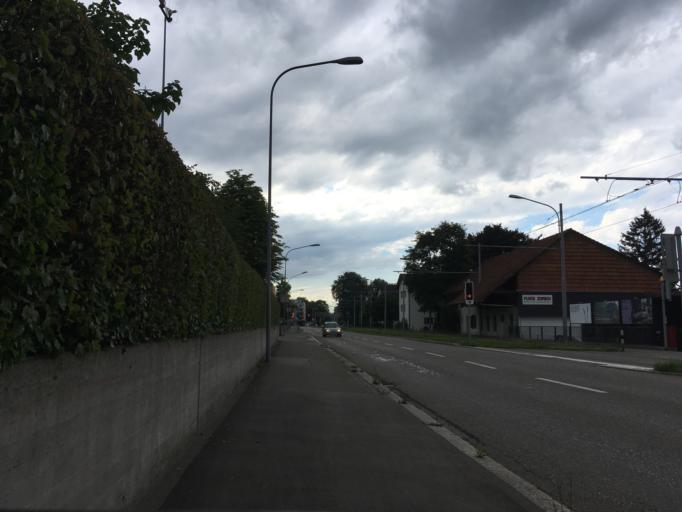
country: CH
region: Zurich
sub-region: Bezirk Zuerich
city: Zuerich (Kreis 12)
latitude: 47.4019
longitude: 8.5805
